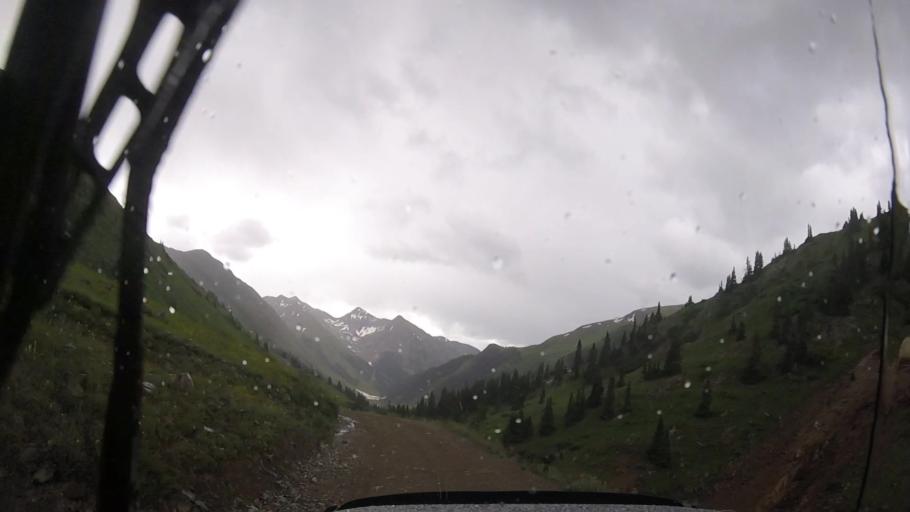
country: US
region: Colorado
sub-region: Ouray County
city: Ouray
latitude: 37.9377
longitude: -107.5724
